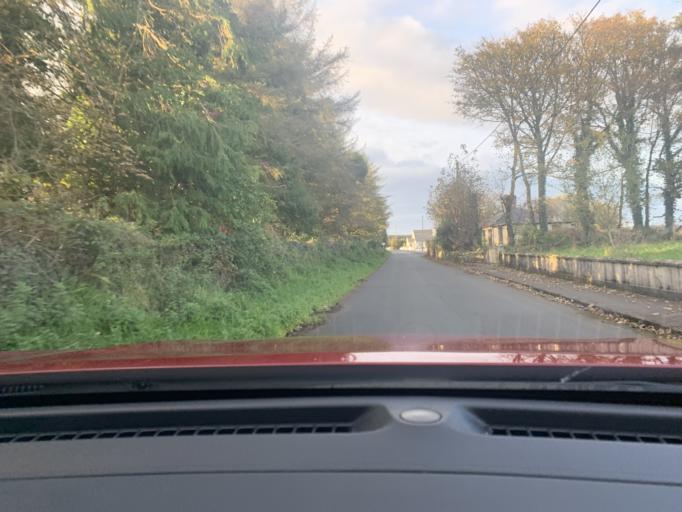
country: IE
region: Connaught
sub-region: Roscommon
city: Ballaghaderreen
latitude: 53.9060
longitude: -8.5779
